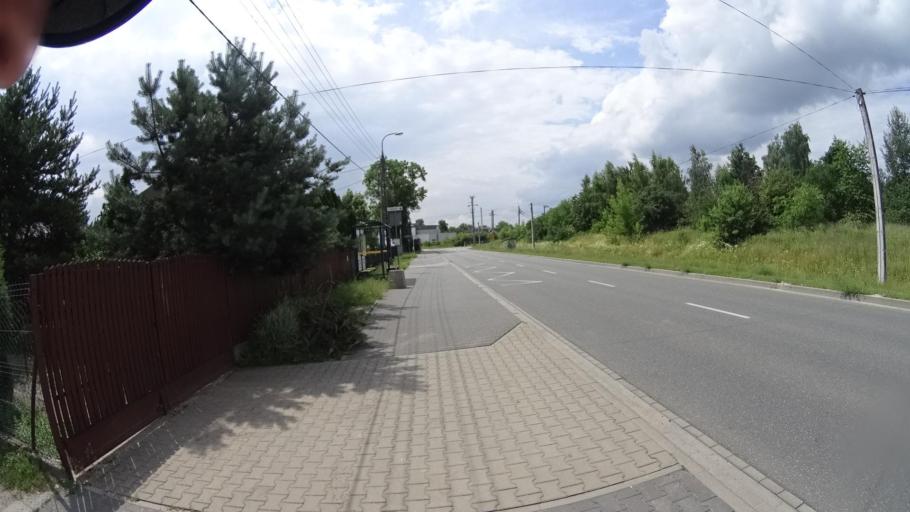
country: PL
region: Masovian Voivodeship
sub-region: Powiat pruszkowski
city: Pruszkow
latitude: 52.1714
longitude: 20.7763
